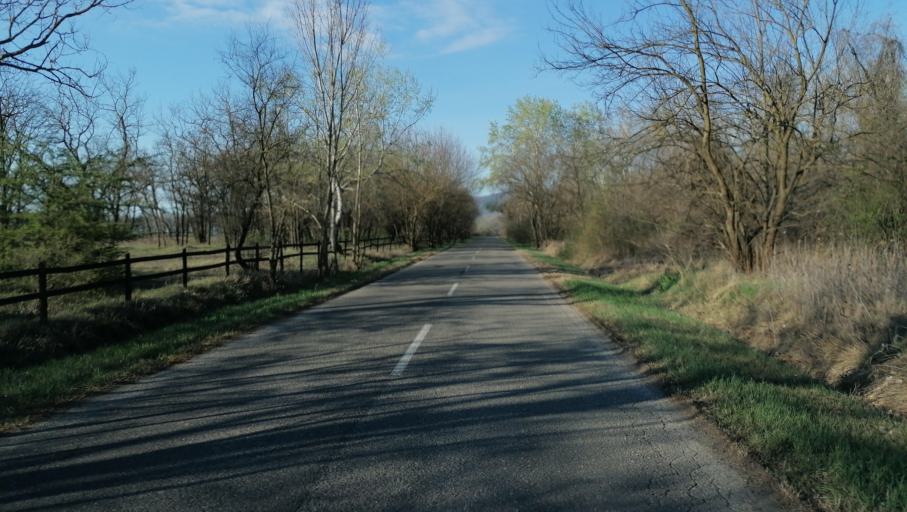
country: HU
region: Pest
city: Tahitotfalu
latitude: 47.7686
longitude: 19.1117
